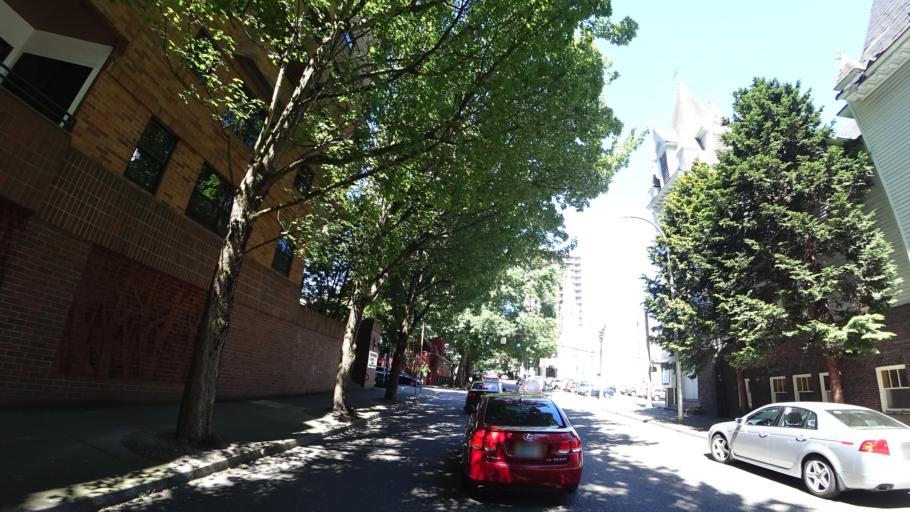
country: US
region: Oregon
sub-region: Multnomah County
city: Portland
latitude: 45.5146
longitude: -122.6845
